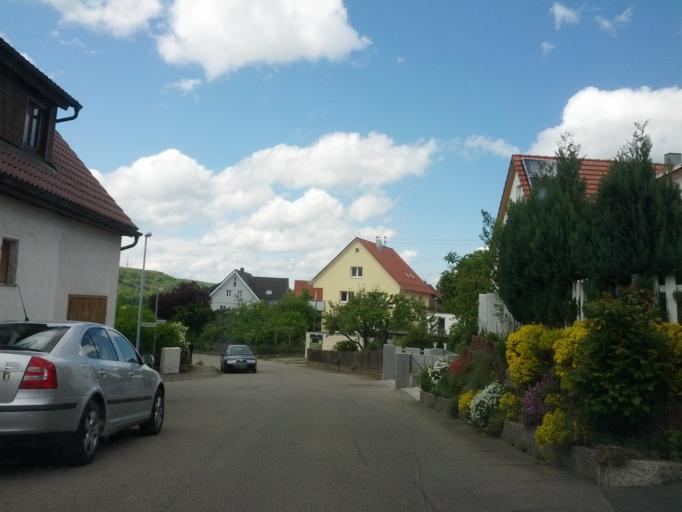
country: DE
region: Baden-Wuerttemberg
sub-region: Regierungsbezirk Stuttgart
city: Aidlingen
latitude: 48.7131
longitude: 8.9113
